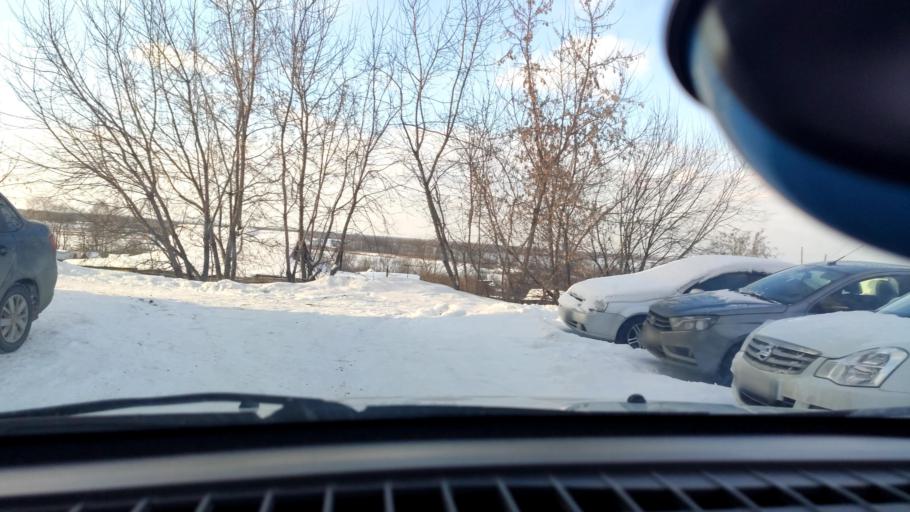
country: RU
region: Perm
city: Kondratovo
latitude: 57.9466
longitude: 56.0666
